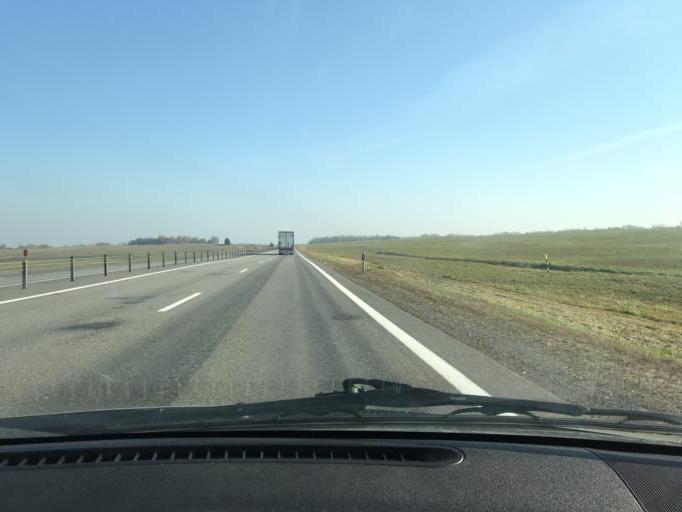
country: BY
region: Vitebsk
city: Dubrowna
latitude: 54.6416
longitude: 30.5843
